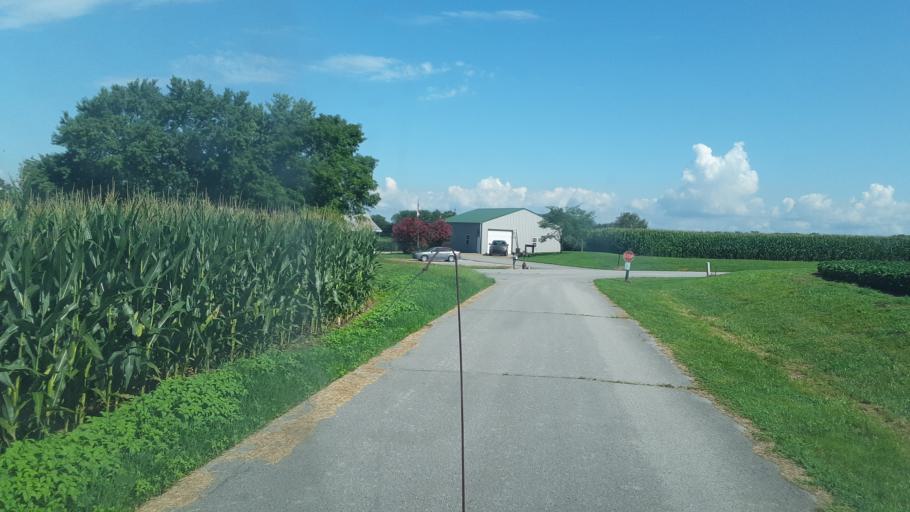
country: US
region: Kentucky
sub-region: Todd County
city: Elkton
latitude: 36.7781
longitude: -87.2340
